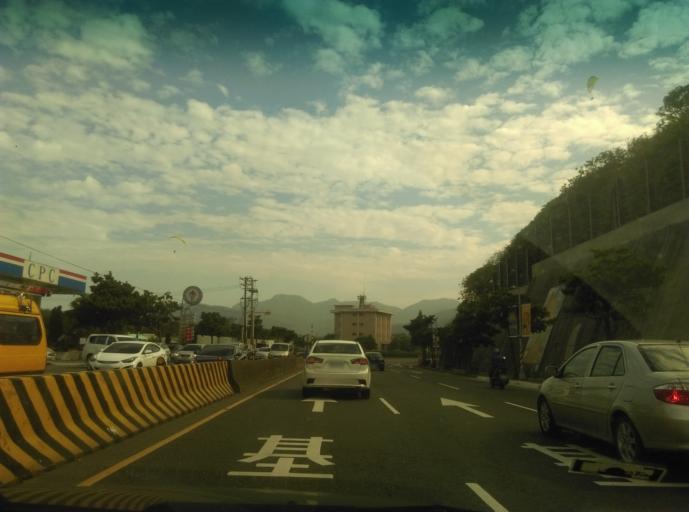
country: TW
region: Taiwan
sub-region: Keelung
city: Keelung
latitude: 25.1845
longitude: 121.6865
